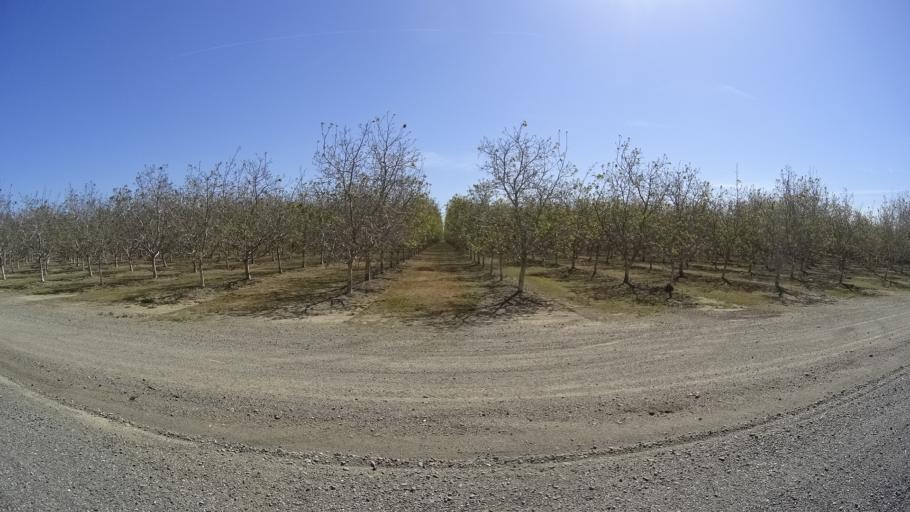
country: US
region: California
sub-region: Glenn County
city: Willows
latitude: 39.6330
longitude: -122.1040
